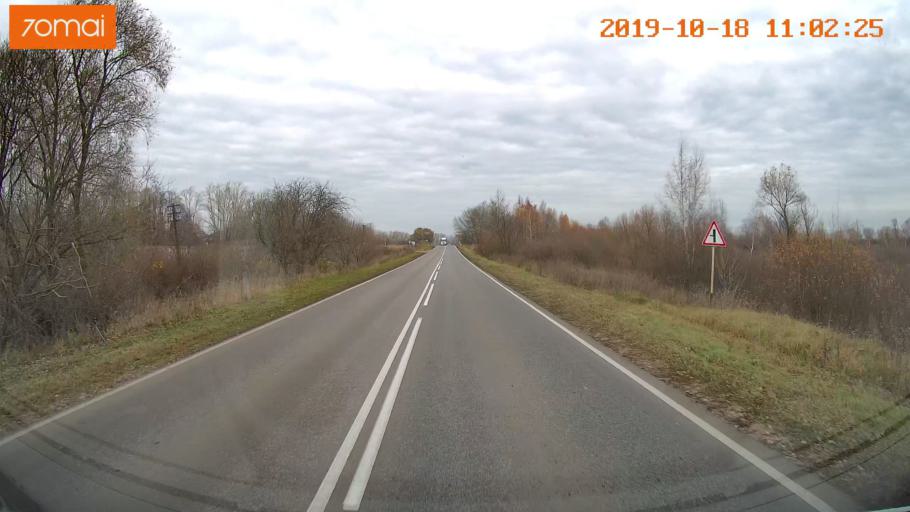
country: RU
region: Tula
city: Yepifan'
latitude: 53.8652
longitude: 38.5448
